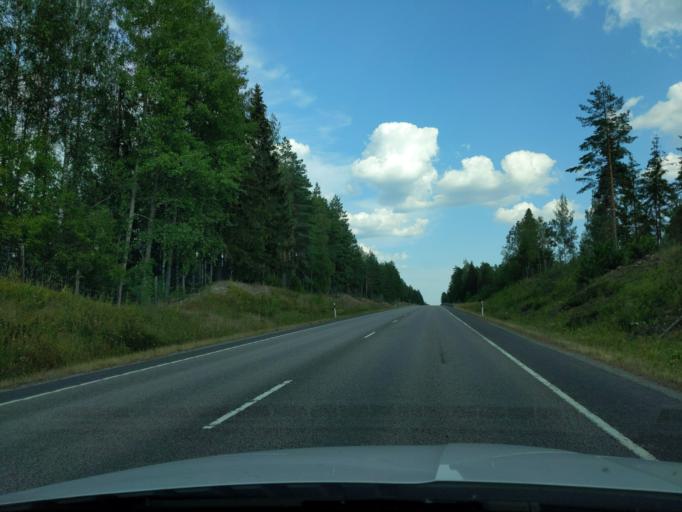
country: FI
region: Paijanne Tavastia
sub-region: Lahti
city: Hollola
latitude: 60.9974
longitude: 25.3509
